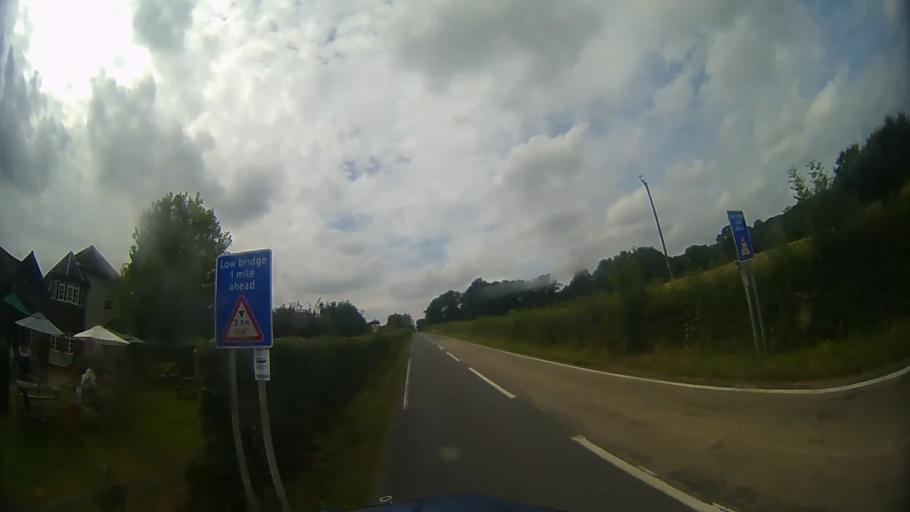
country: GB
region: England
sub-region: Hampshire
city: Kingsley
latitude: 51.1677
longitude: -0.8592
